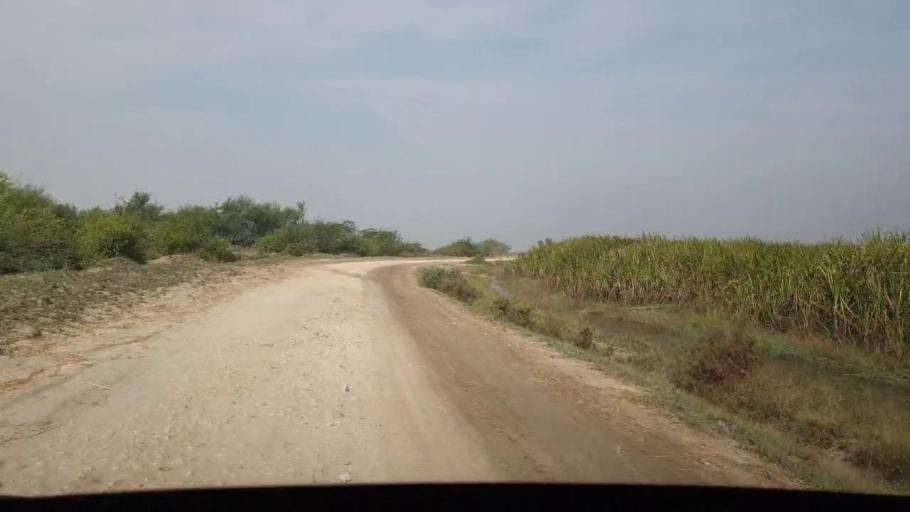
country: PK
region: Sindh
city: Chuhar Jamali
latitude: 24.3207
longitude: 67.9475
